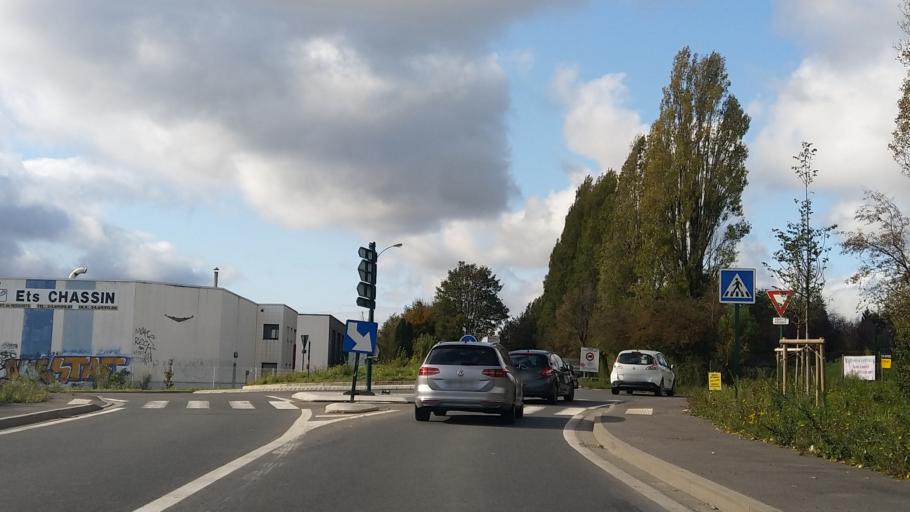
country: FR
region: Ile-de-France
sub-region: Departement du Val-d'Oise
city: Montsoult
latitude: 49.0638
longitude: 2.3265
